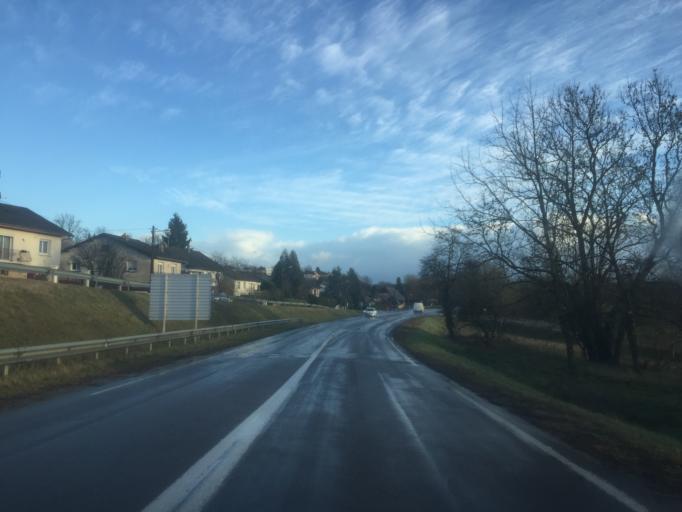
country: FR
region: Franche-Comte
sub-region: Departement du Jura
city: Dampierre
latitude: 47.1503
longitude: 5.7192
